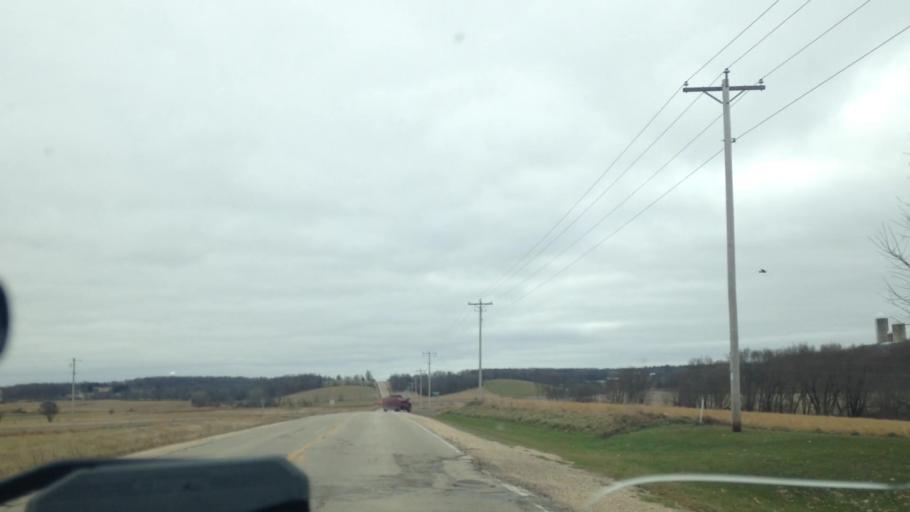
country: US
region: Wisconsin
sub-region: Dodge County
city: Mayville
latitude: 43.4726
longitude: -88.4998
